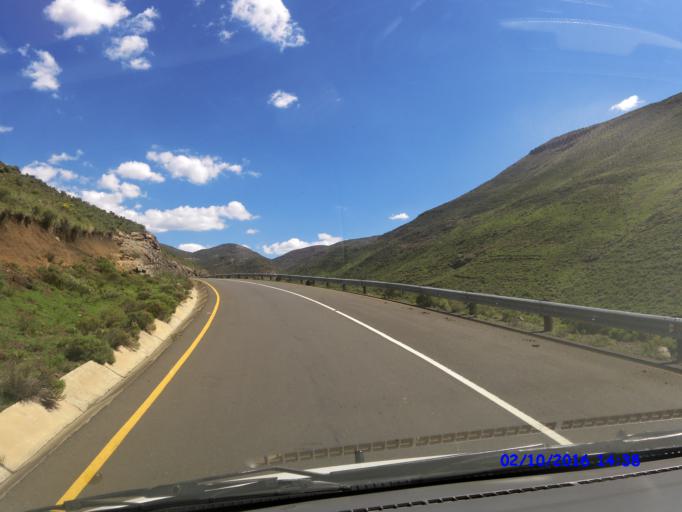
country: LS
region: Maseru
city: Nako
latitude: -29.5107
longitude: 28.0631
